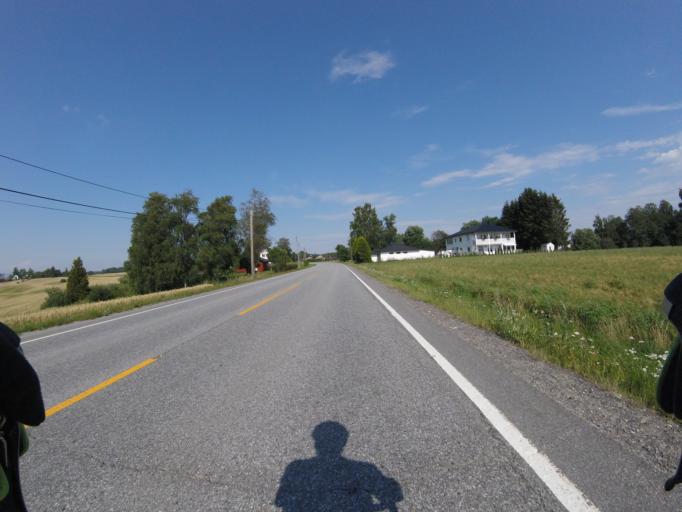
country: NO
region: Akershus
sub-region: Sorum
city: Frogner
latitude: 60.0436
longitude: 11.1164
